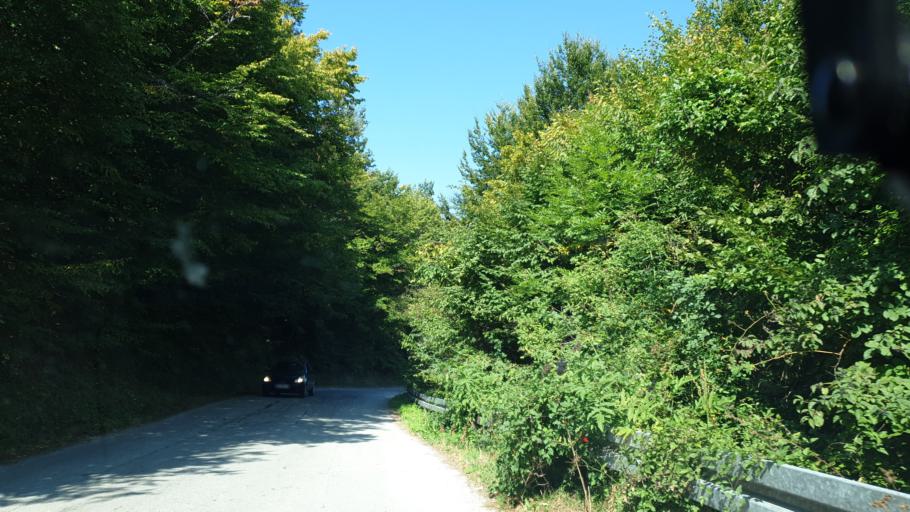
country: RS
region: Central Serbia
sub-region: Zlatiborski Okrug
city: Cajetina
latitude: 43.7018
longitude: 19.8475
